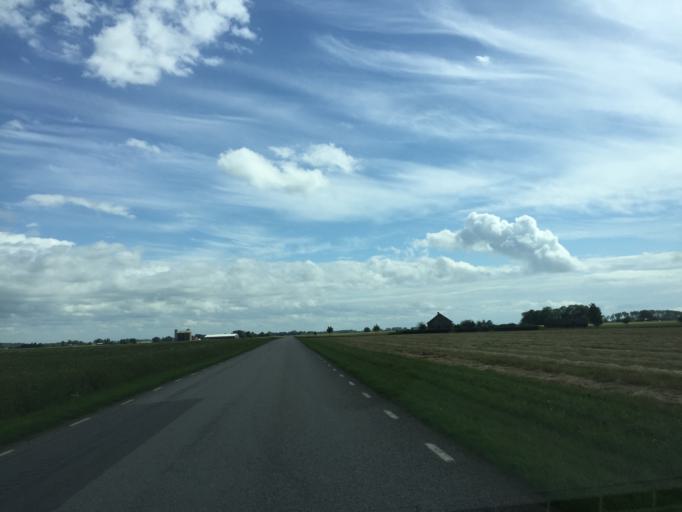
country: SE
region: OEstergoetland
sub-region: Vadstena Kommun
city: Vadstena
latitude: 58.4442
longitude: 14.8425
